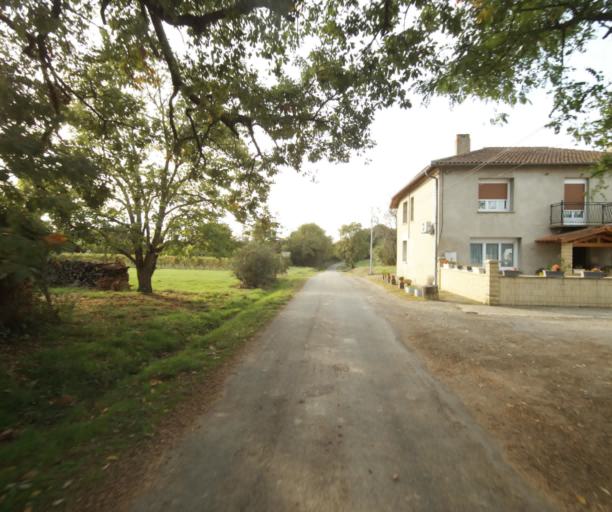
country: FR
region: Midi-Pyrenees
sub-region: Departement du Tarn-et-Garonne
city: Campsas
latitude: 43.8710
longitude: 1.3360
